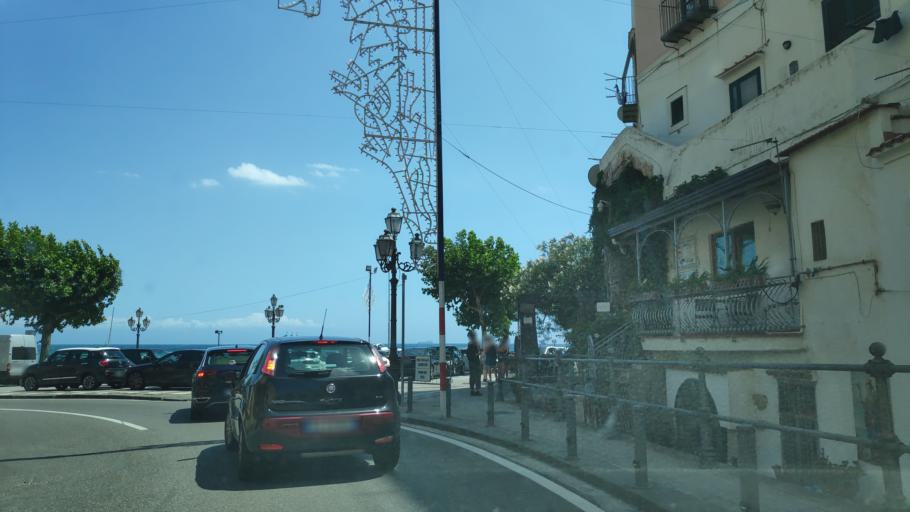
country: IT
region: Campania
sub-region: Provincia di Salerno
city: Minori
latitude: 40.6494
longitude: 14.6261
